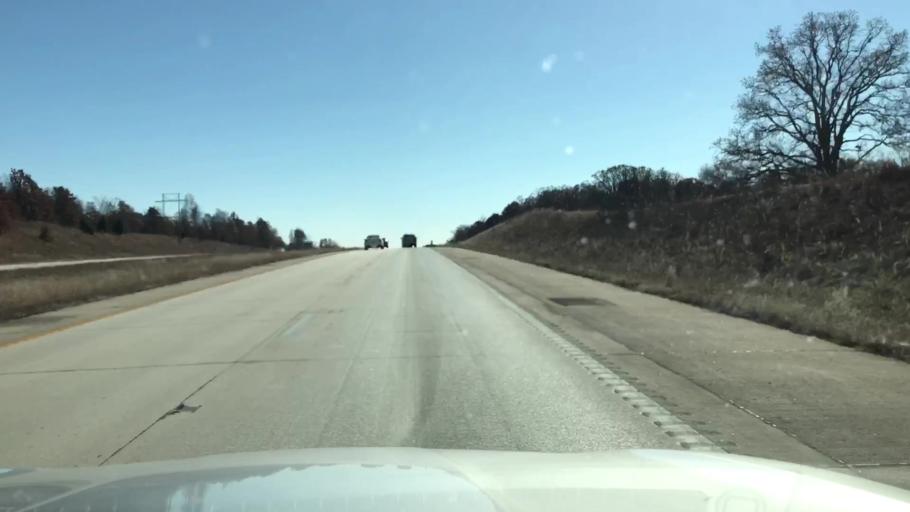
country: US
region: Missouri
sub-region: Jasper County
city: Duquesne
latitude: 37.0253
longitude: -94.4301
